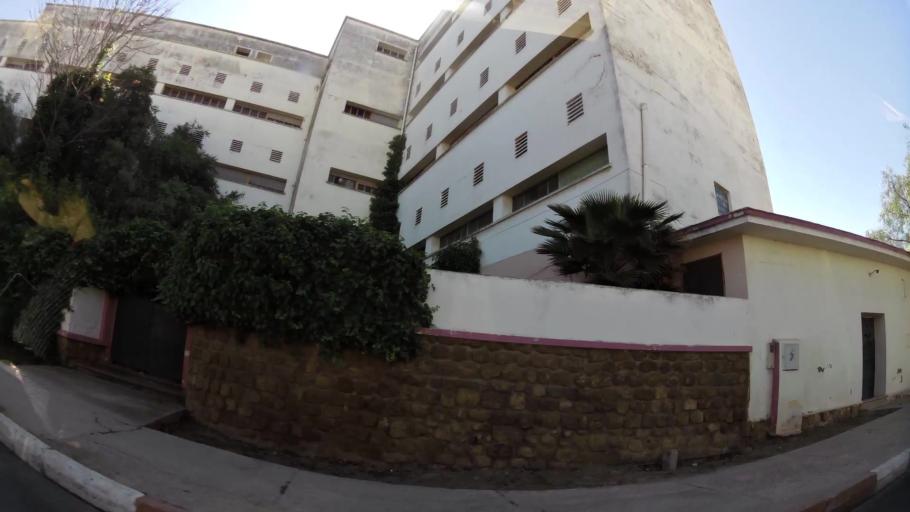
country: MA
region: Meknes-Tafilalet
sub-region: Meknes
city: Meknes
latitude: 33.9045
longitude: -5.5468
